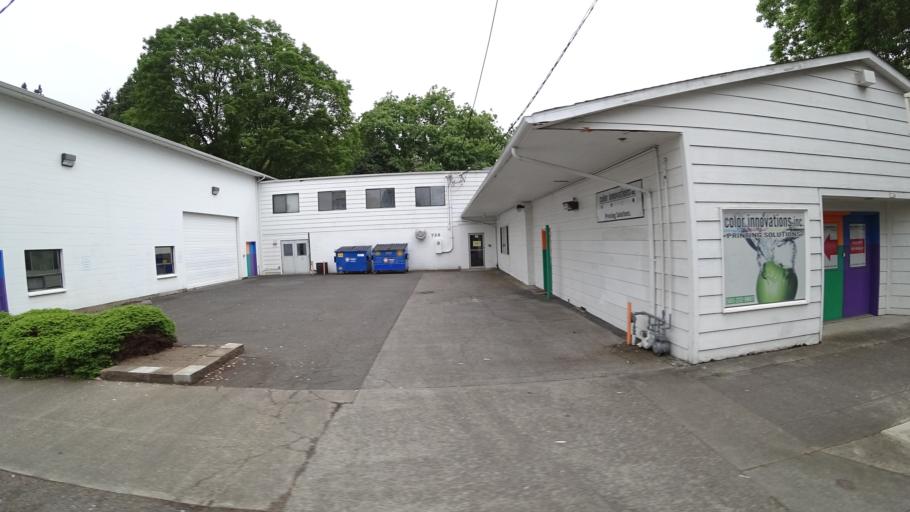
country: US
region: Oregon
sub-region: Multnomah County
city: Portland
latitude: 45.5175
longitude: -122.6455
